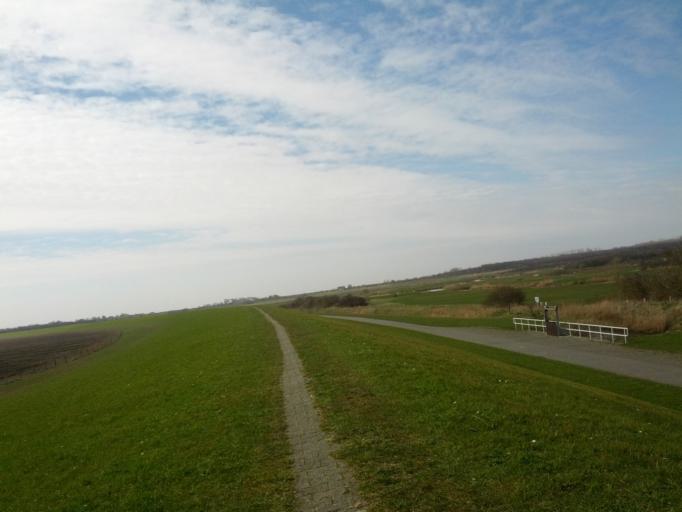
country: DE
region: Lower Saxony
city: Langeoog
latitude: 53.7418
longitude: 7.5050
